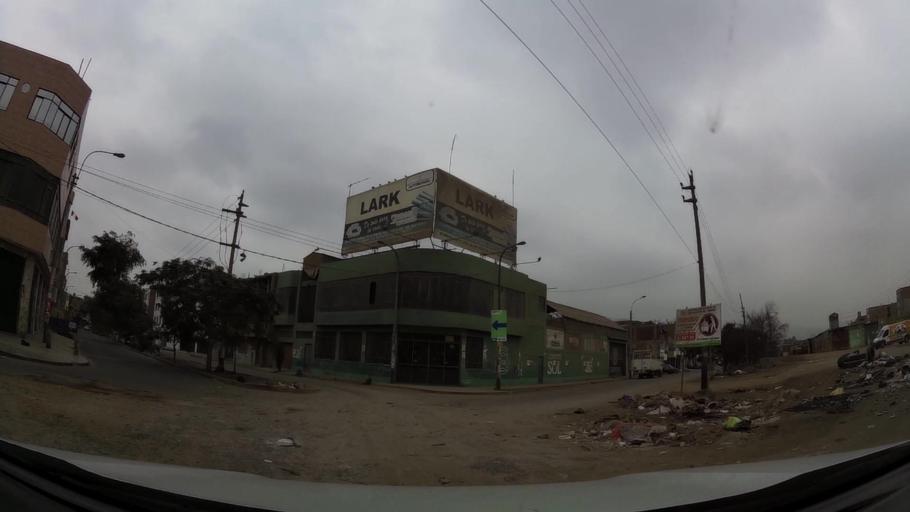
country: PE
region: Lima
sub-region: Lima
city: Independencia
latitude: -11.9495
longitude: -77.0860
